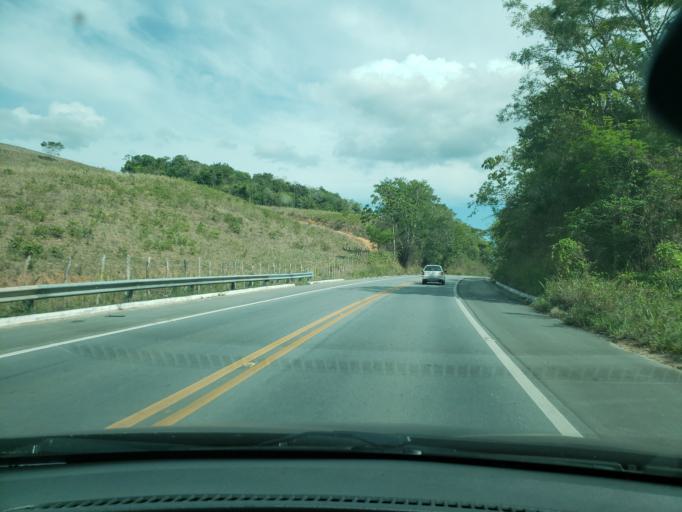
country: BR
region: Alagoas
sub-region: Murici
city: Murici
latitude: -9.3288
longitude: -35.9175
